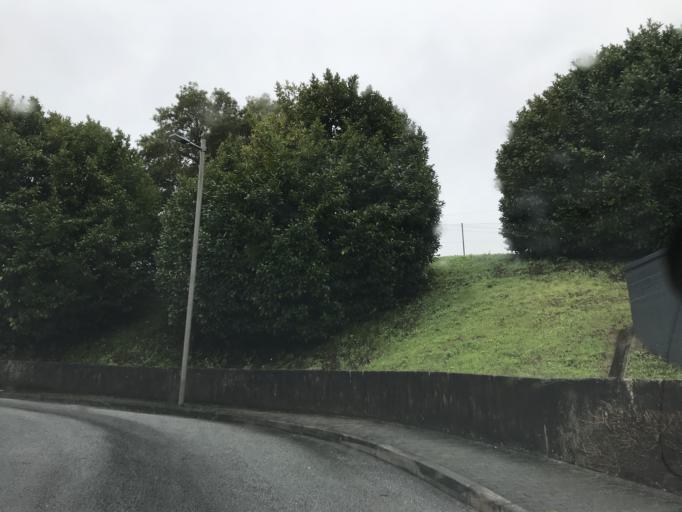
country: PT
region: Braga
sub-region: Vila Nova de Famalicao
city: Vila Nova de Famalicao
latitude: 41.4123
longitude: -8.5139
